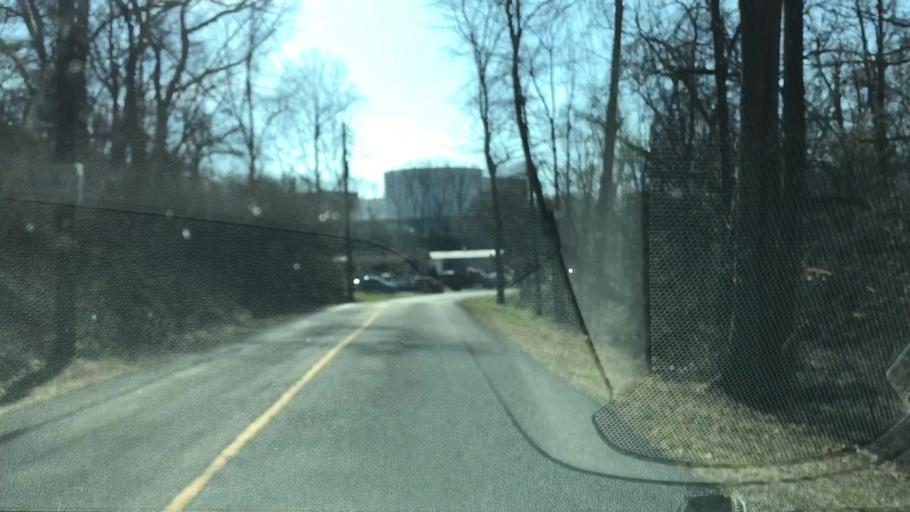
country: US
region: Pennsylvania
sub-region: Dauphin County
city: Highspire
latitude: 40.2219
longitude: -76.7959
